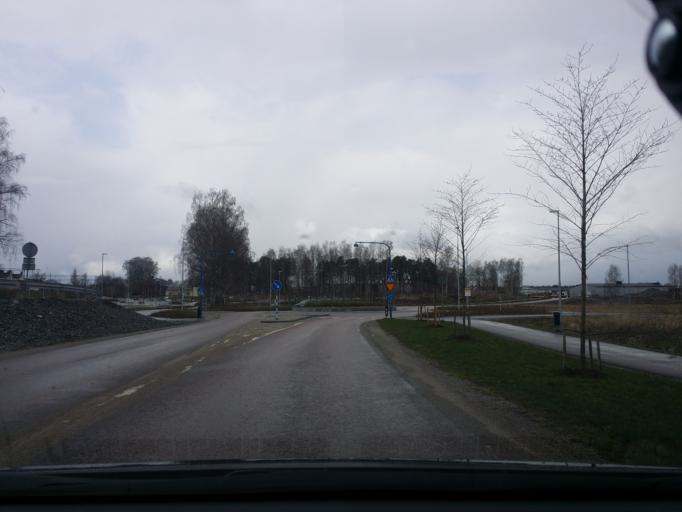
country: SE
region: Uppsala
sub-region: Enkopings Kommun
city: Enkoping
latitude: 59.6448
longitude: 17.0955
